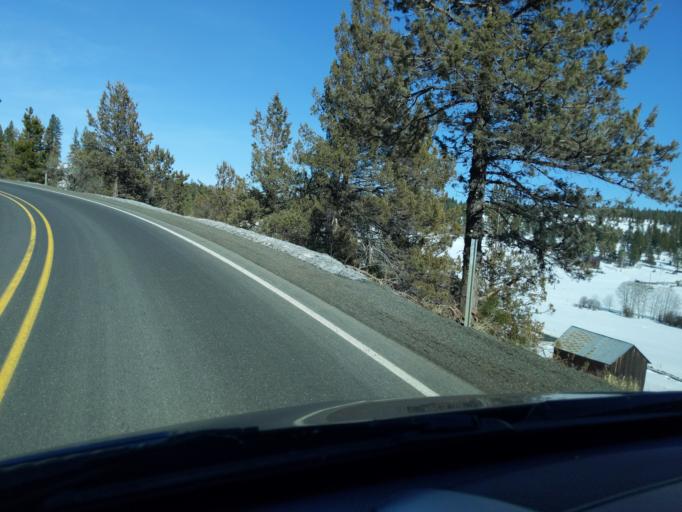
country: US
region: Oregon
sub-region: Grant County
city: John Day
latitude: 44.9050
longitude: -119.0112
